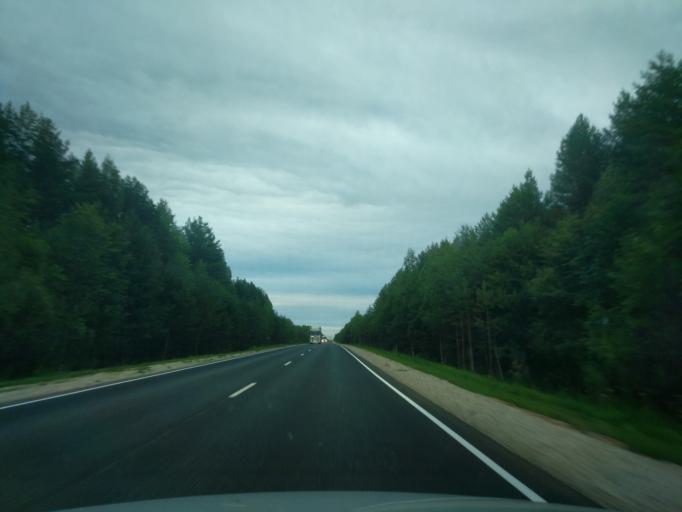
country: RU
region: Kostroma
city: Ponazyrevo
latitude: 58.3238
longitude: 46.5073
